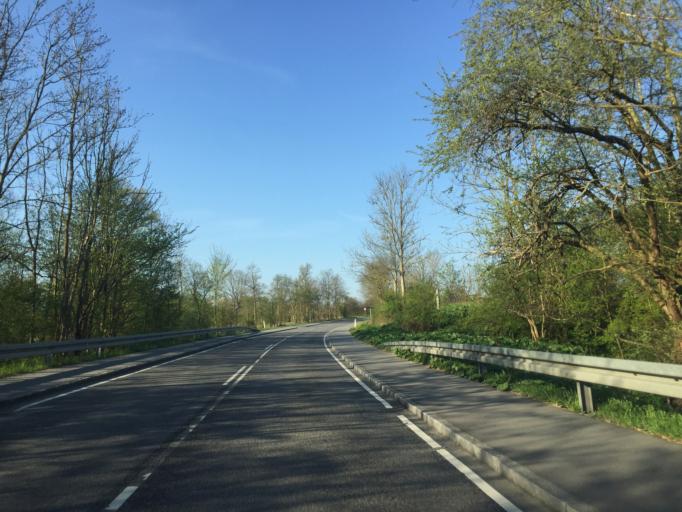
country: DK
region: South Denmark
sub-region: Svendborg Kommune
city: Thuro By
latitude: 55.1004
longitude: 10.7076
